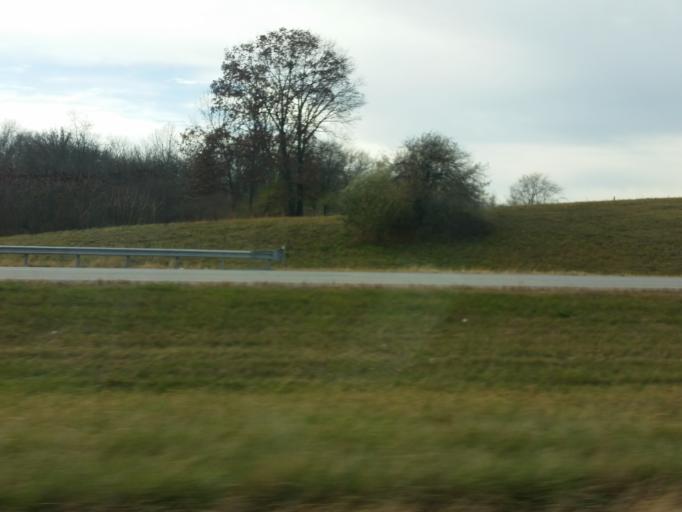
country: US
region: Illinois
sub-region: Henry County
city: Green Rock
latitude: 41.4488
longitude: -90.3694
